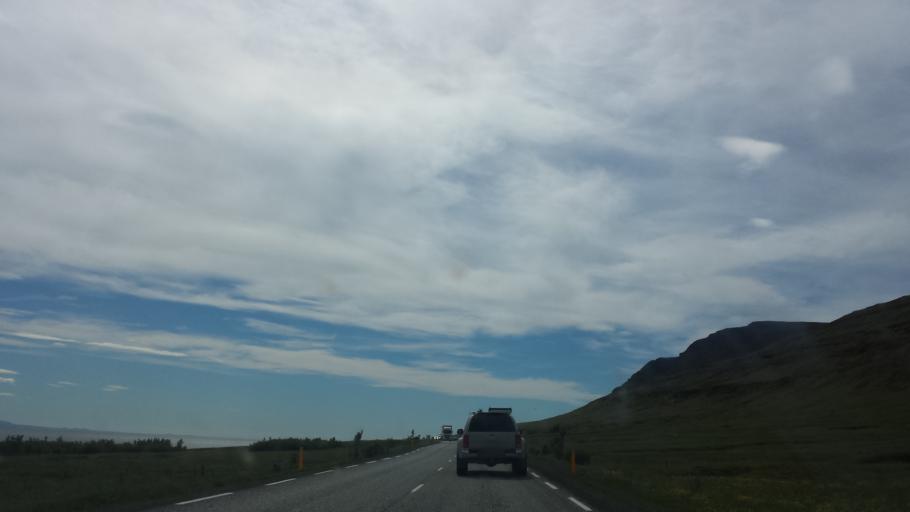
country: IS
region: Capital Region
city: Reykjavik
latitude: 64.3383
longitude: -21.8297
